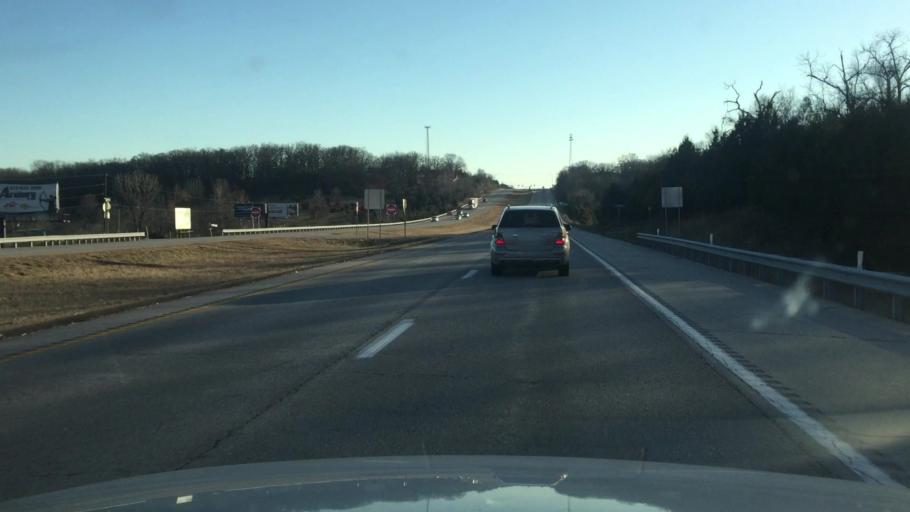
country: US
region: Missouri
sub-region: Cole County
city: Wardsville
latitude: 38.4914
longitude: -92.2701
